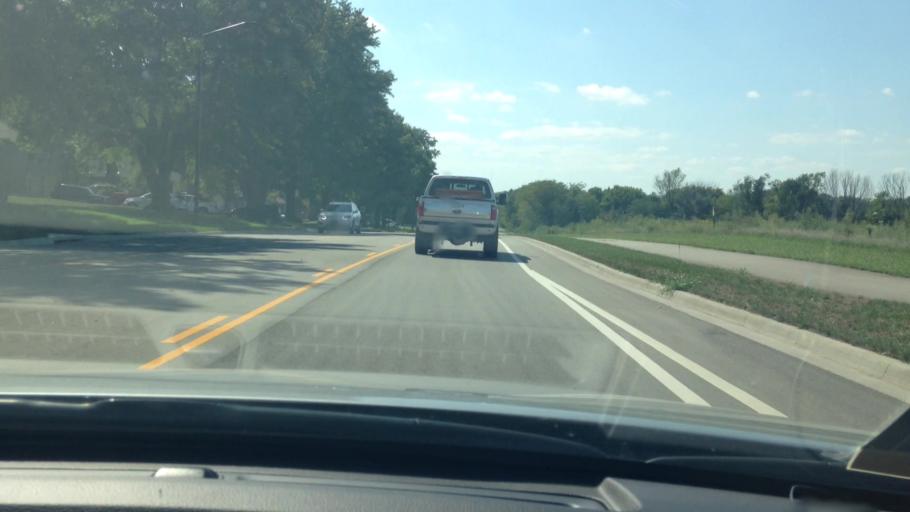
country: US
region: Kansas
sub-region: Johnson County
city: Lenexa
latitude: 38.8692
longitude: -94.7257
